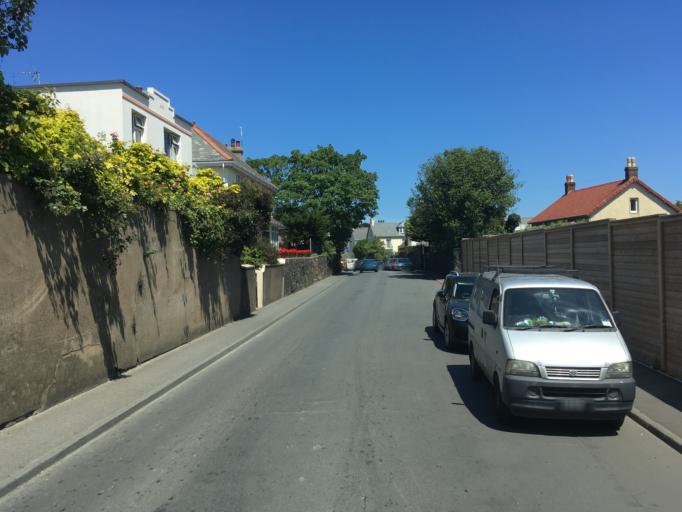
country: GG
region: St Peter Port
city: Saint Peter Port
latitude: 49.4847
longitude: -2.5192
